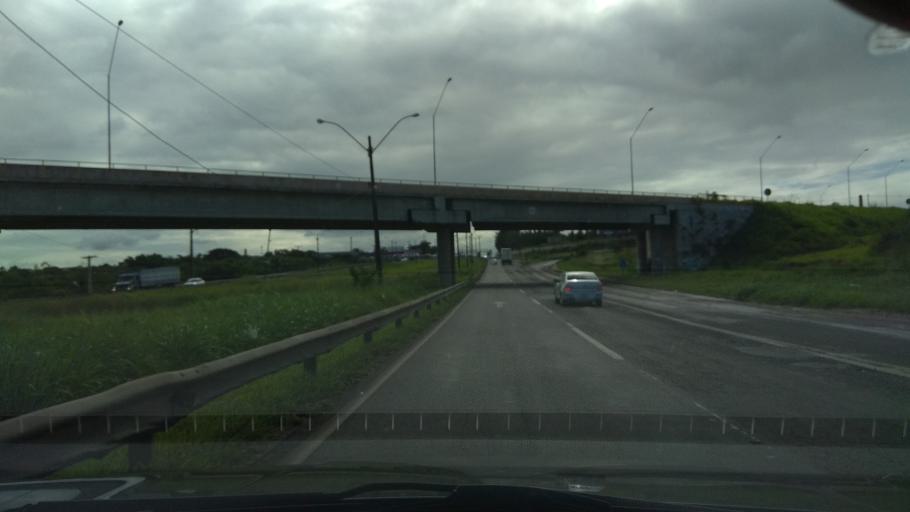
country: BR
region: Bahia
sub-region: Feira De Santana
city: Feira de Santana
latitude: -12.3005
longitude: -38.8984
